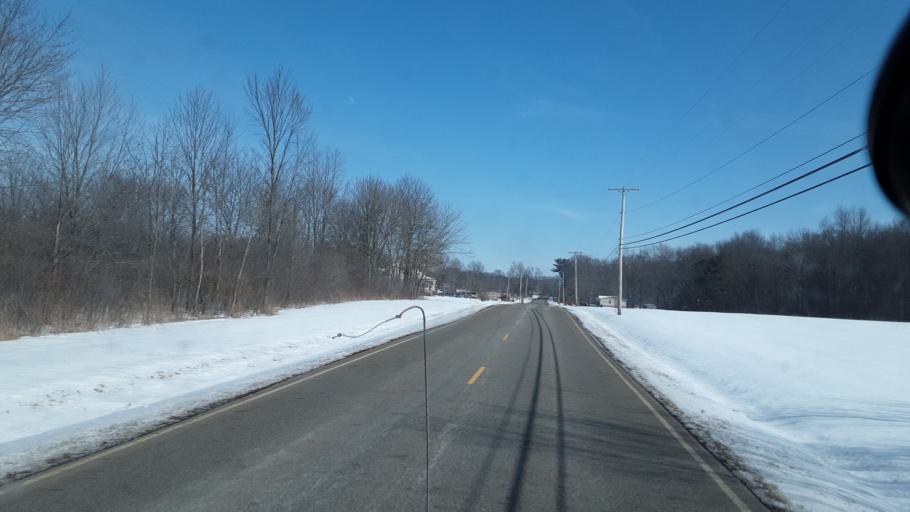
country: US
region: Ohio
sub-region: Stark County
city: Alliance
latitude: 40.9623
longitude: -81.1021
